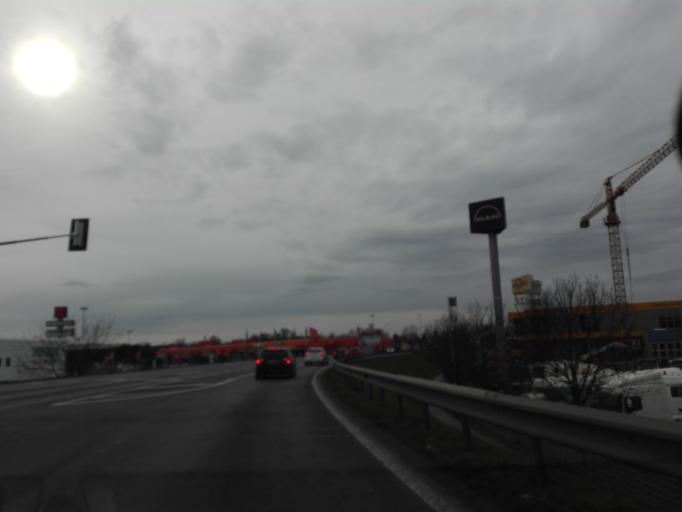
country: AT
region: Upper Austria
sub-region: Politischer Bezirk Linz-Land
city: Ansfelden
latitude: 48.2123
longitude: 14.2759
